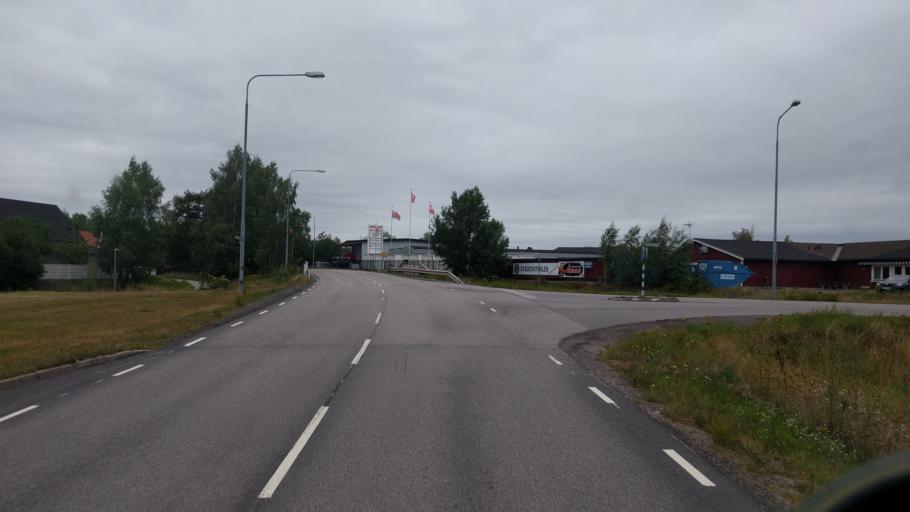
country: SE
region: Kalmar
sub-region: Vasterviks Kommun
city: Vaestervik
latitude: 57.7586
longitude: 16.6087
